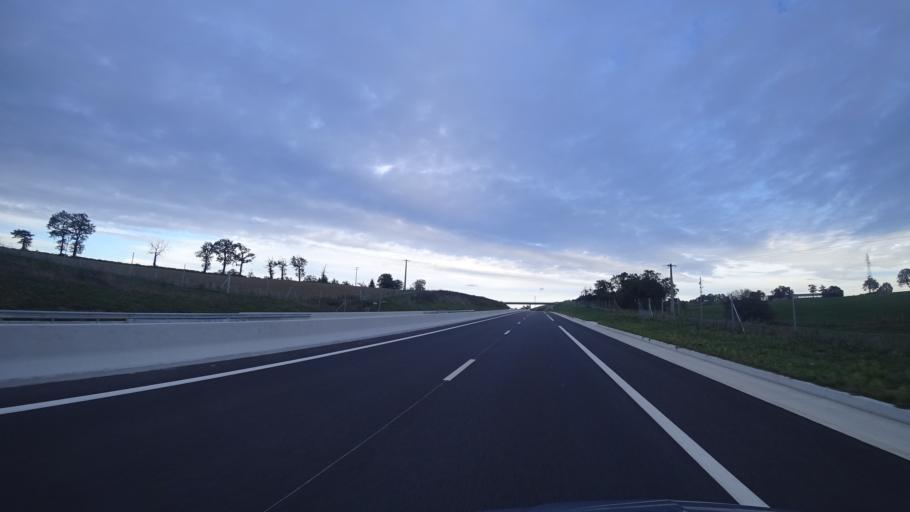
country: FR
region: Midi-Pyrenees
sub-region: Departement de l'Aveyron
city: Baraqueville
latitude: 44.2892
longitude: 2.4649
